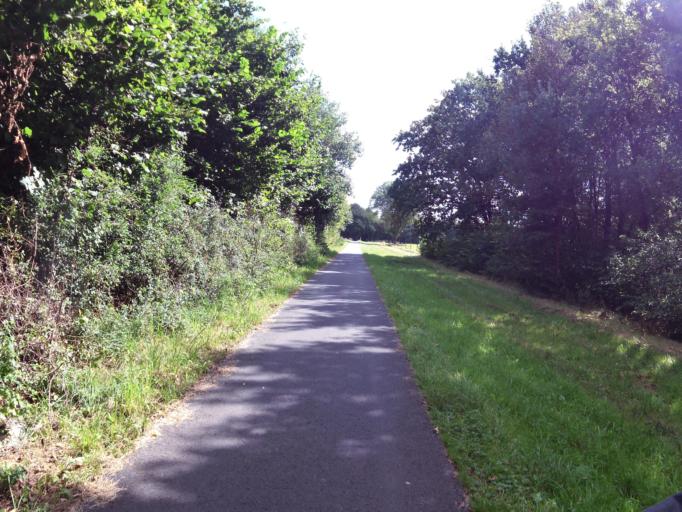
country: NL
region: Drenthe
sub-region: Gemeente Aa en Hunze
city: Anloo
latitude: 52.9891
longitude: 6.7136
